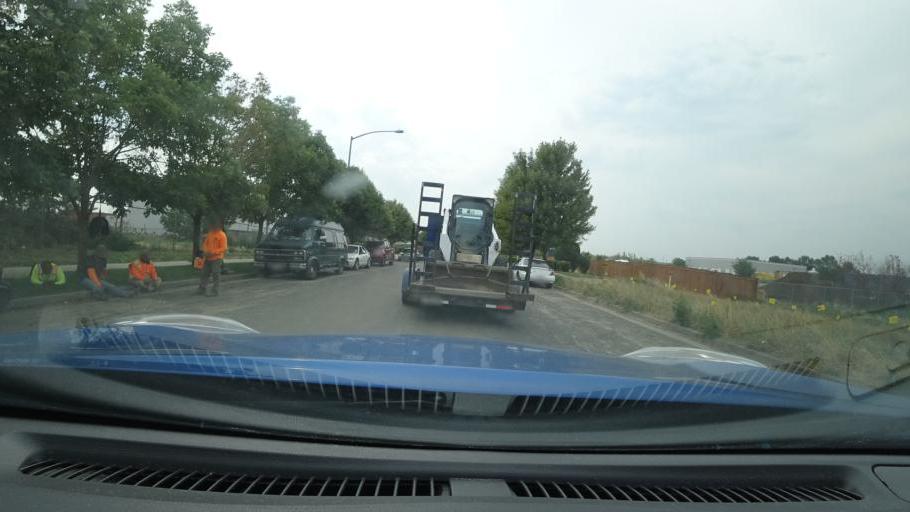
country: US
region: Colorado
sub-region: Adams County
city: Aurora
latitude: 39.7501
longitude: -104.7821
